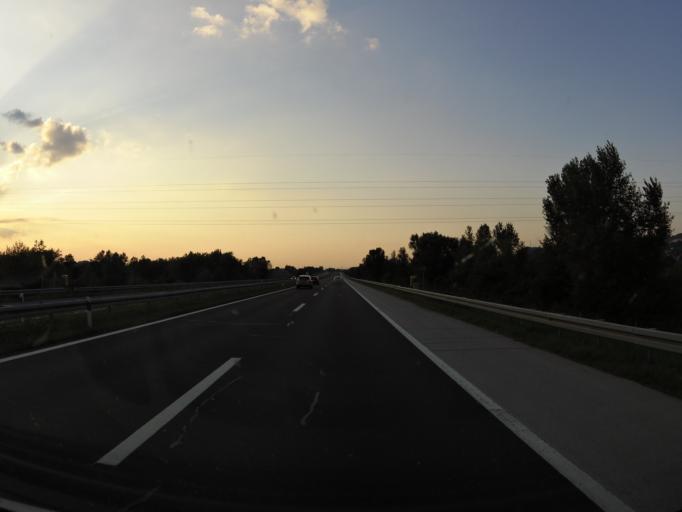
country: HR
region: Zagrebacka
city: Rakitje
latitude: 45.8056
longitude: 15.8351
